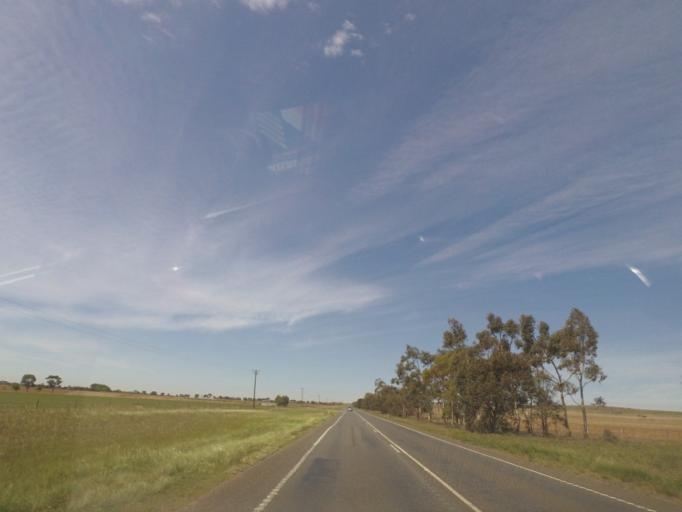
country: AU
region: Victoria
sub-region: Moorabool
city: Bacchus Marsh
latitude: -37.7585
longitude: 144.4414
